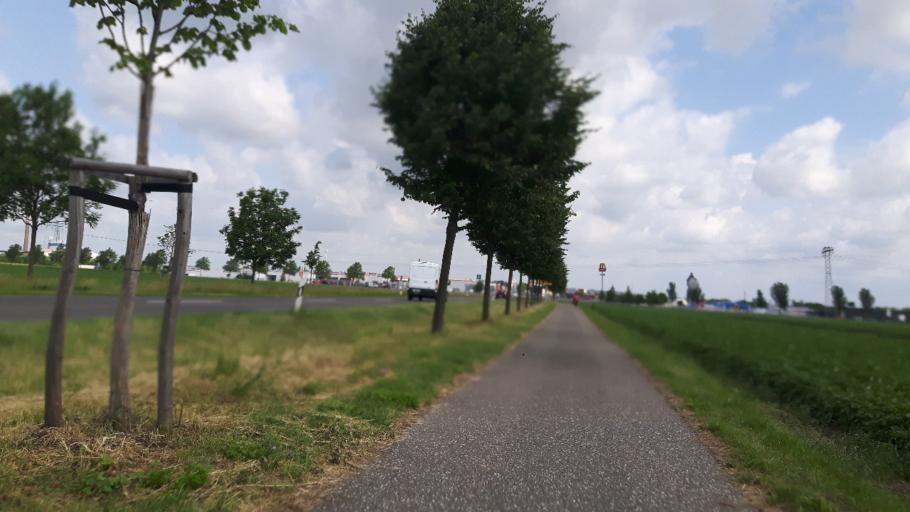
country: DE
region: Saxony
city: Dobernitz
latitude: 51.5082
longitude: 12.3388
